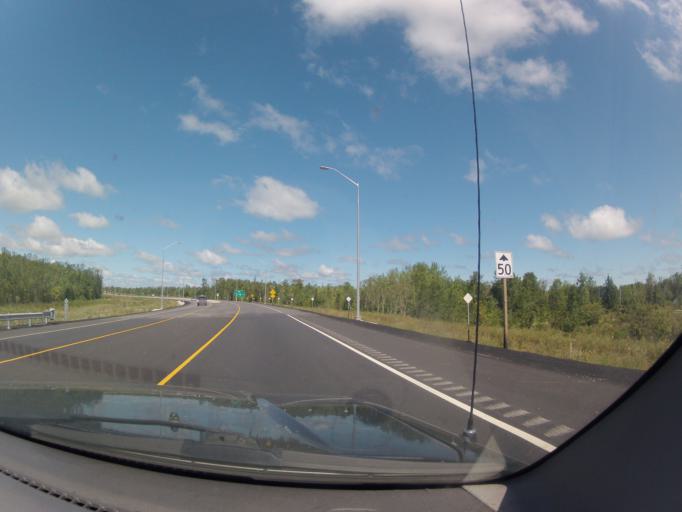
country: CA
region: Ontario
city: Wasaga Beach
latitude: 44.4591
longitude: -80.1062
